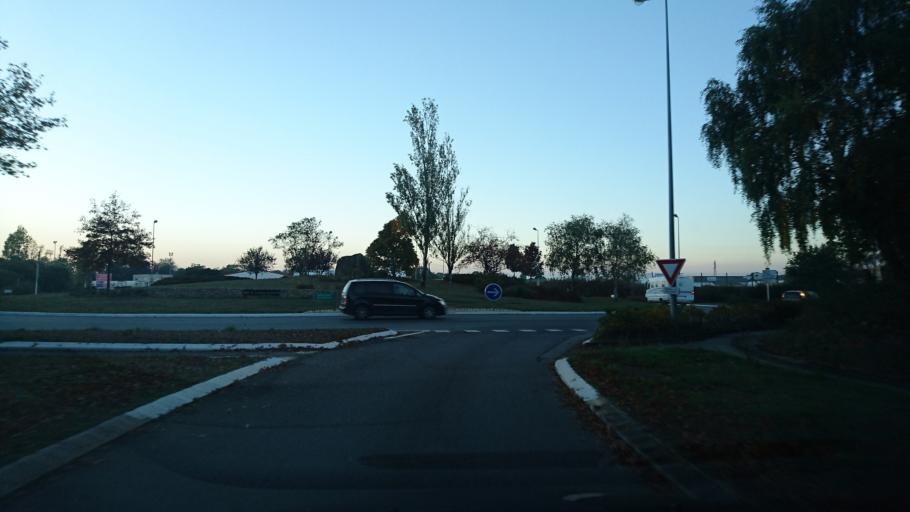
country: FR
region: Brittany
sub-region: Departement du Morbihan
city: Auray
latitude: 47.6829
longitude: -3.0178
